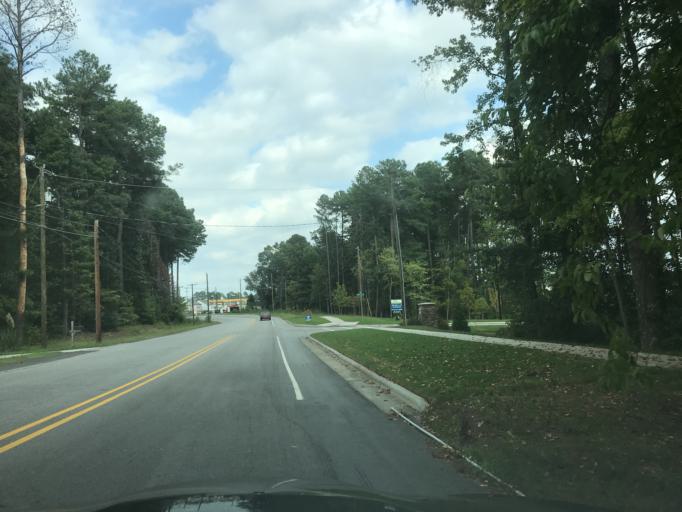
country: US
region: North Carolina
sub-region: Durham County
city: Durham
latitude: 35.9044
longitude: -78.9197
